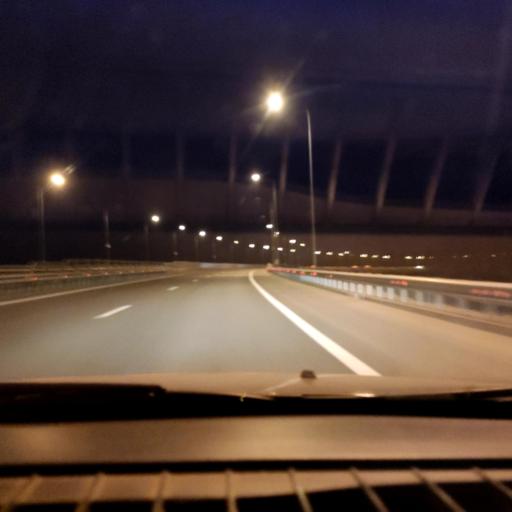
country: RU
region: Samara
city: Bereza
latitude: 53.4994
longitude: 50.1166
